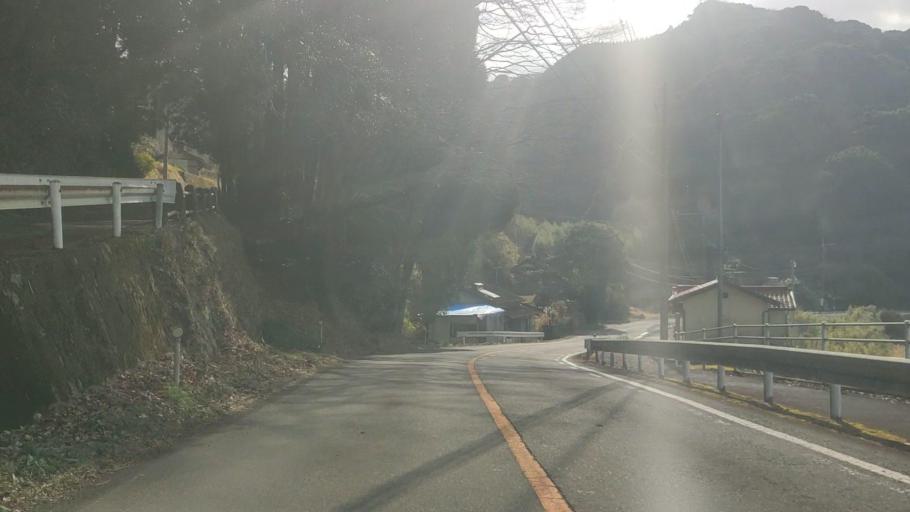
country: JP
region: Kumamoto
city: Hitoyoshi
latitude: 32.2881
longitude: 130.8464
